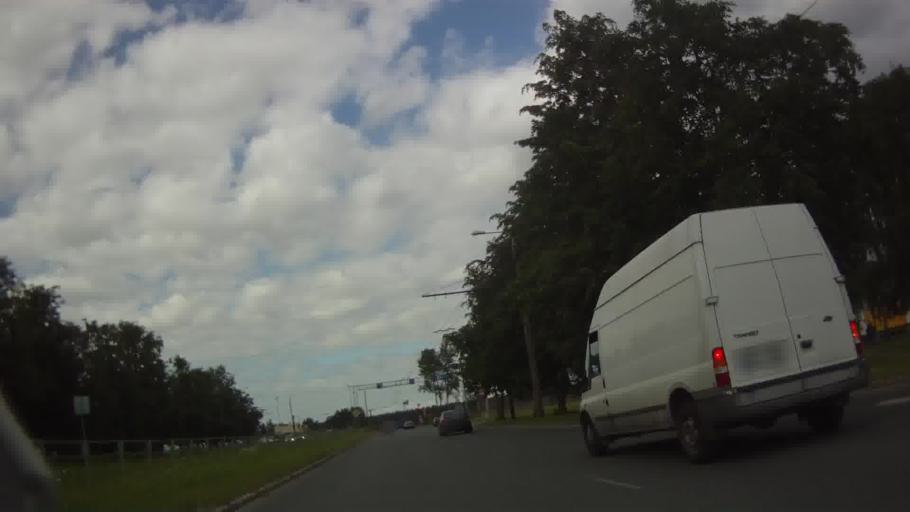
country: LV
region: Stopini
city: Ulbroka
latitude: 56.9449
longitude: 24.2066
